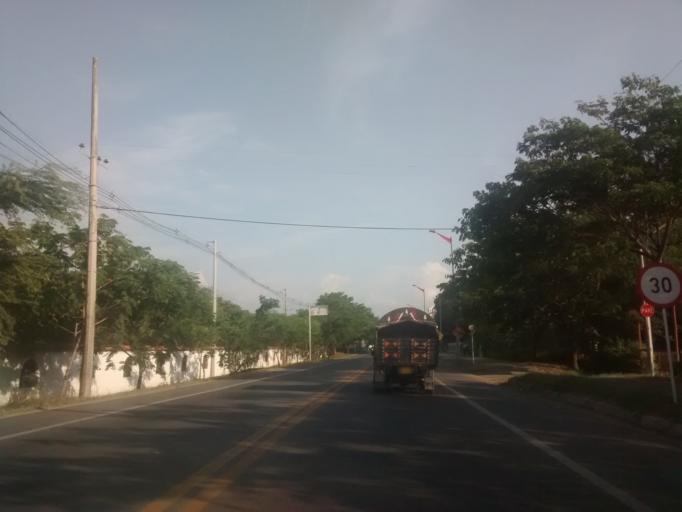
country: CO
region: Cundinamarca
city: Ricaurte
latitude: 4.2910
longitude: -74.7790
